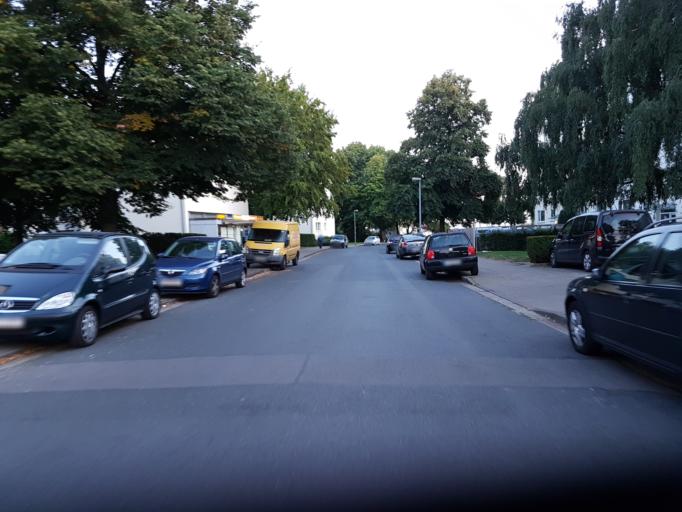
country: DE
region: Lower Saxony
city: Langenhagen
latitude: 52.4131
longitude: 9.7564
